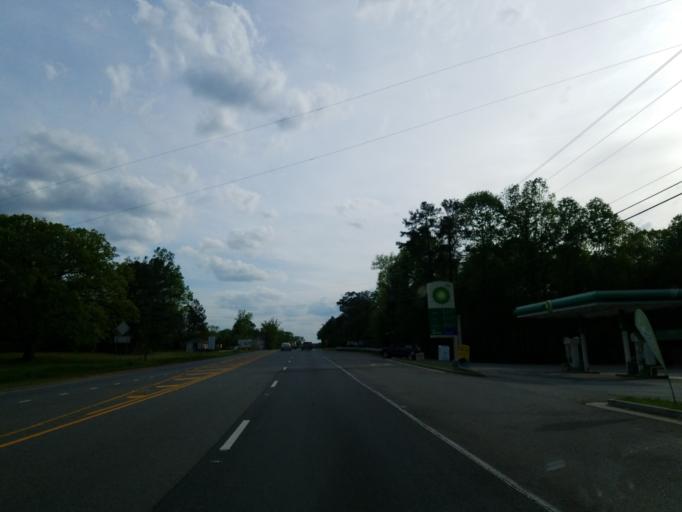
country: US
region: Georgia
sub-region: Cherokee County
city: Ball Ground
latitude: 34.2481
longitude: -84.3782
